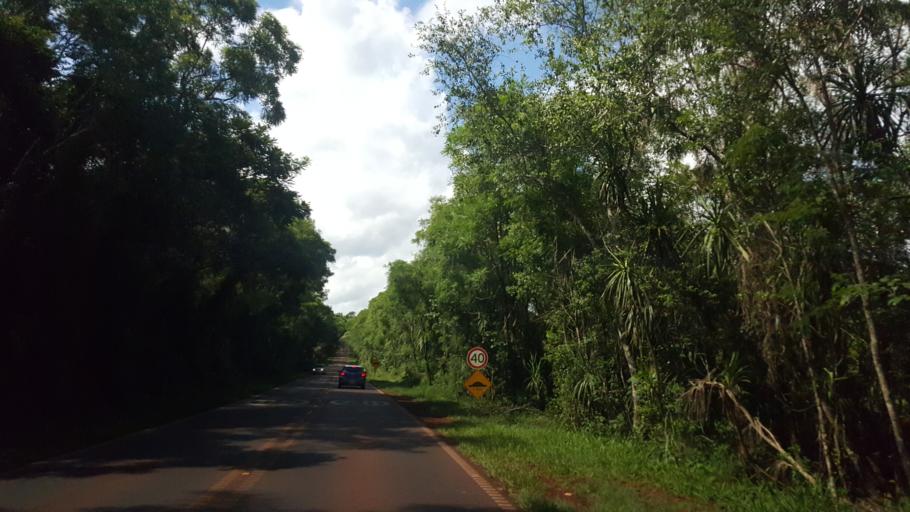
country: AR
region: Misiones
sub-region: Departamento de Iguazu
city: Puerto Iguazu
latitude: -25.7182
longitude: -54.4624
